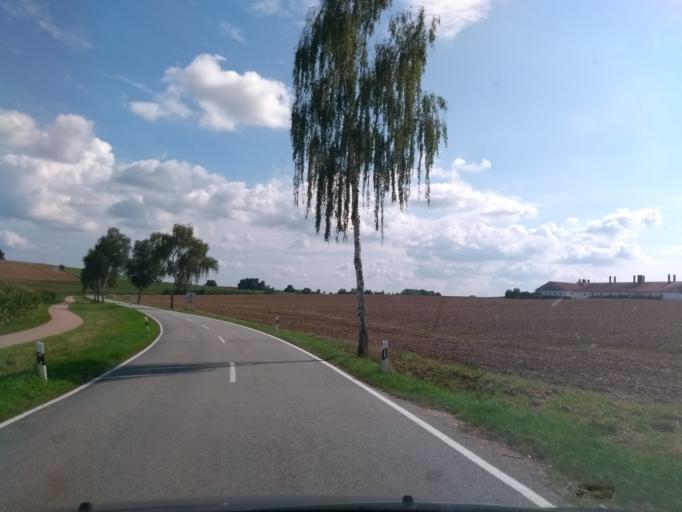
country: DE
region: Bavaria
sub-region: Upper Bavaria
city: Schwabhausen
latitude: 48.3907
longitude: 11.3503
